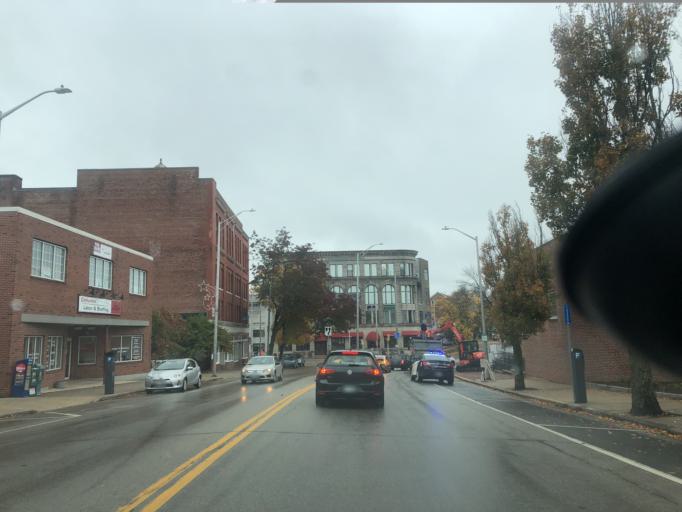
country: US
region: New Hampshire
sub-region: Strafford County
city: Dover
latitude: 43.1940
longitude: -70.8747
